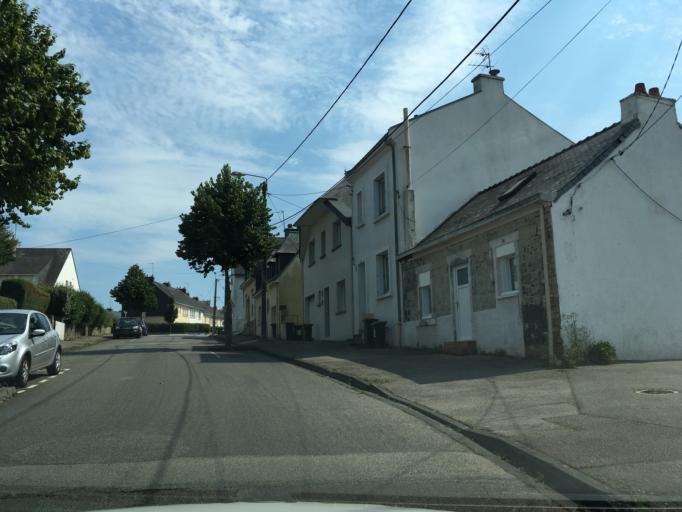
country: FR
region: Brittany
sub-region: Departement du Morbihan
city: Lorient
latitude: 47.7661
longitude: -3.3903
